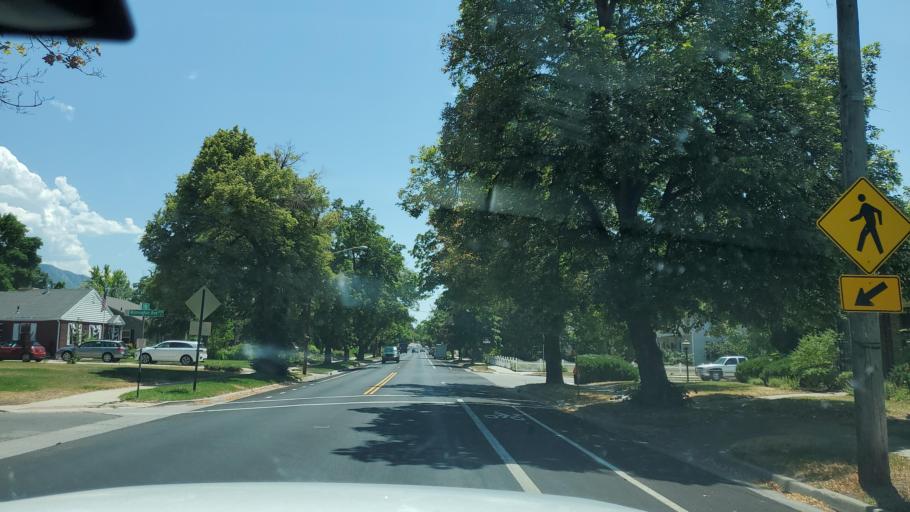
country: US
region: Utah
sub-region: Salt Lake County
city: Willard
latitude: 40.7235
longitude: -111.8309
